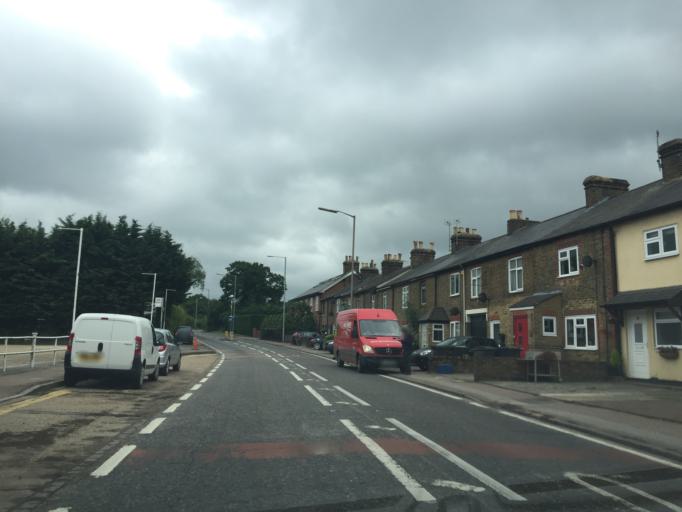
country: GB
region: England
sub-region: Essex
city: Epping
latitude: 51.7210
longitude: 0.1288
